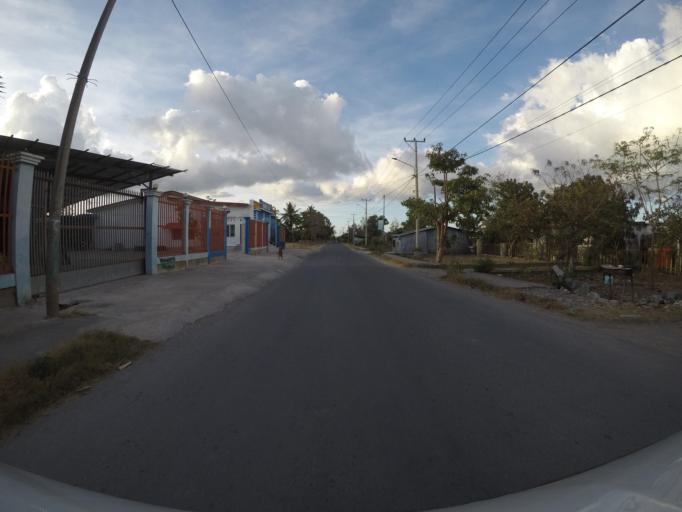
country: TL
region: Baucau
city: Baucau
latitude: -8.4725
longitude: 126.4561
